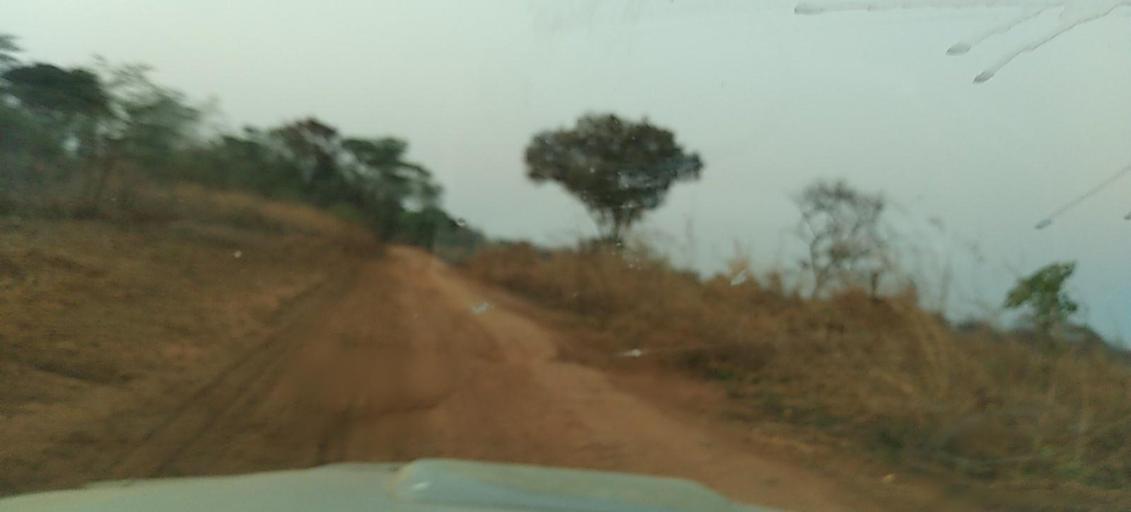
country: ZM
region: North-Western
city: Kasempa
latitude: -13.0650
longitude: 26.3817
